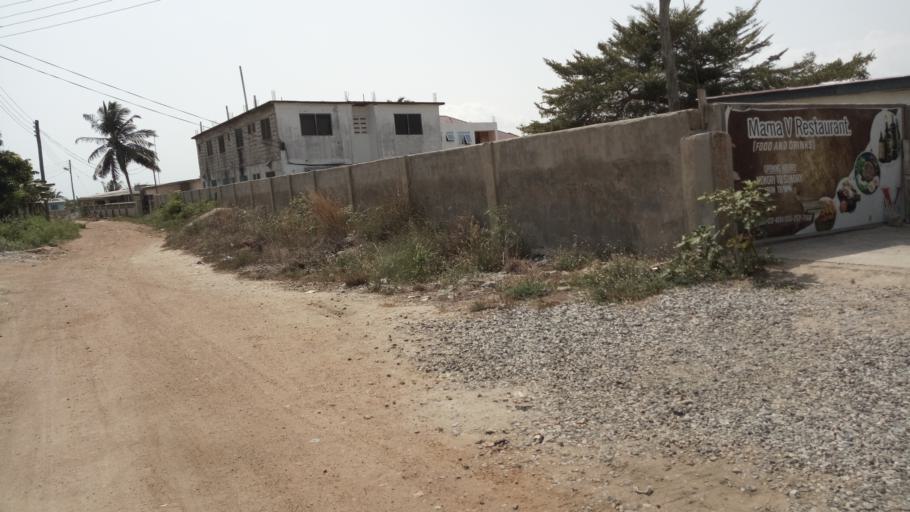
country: GH
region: Central
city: Winneba
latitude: 5.3620
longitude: -0.6369
